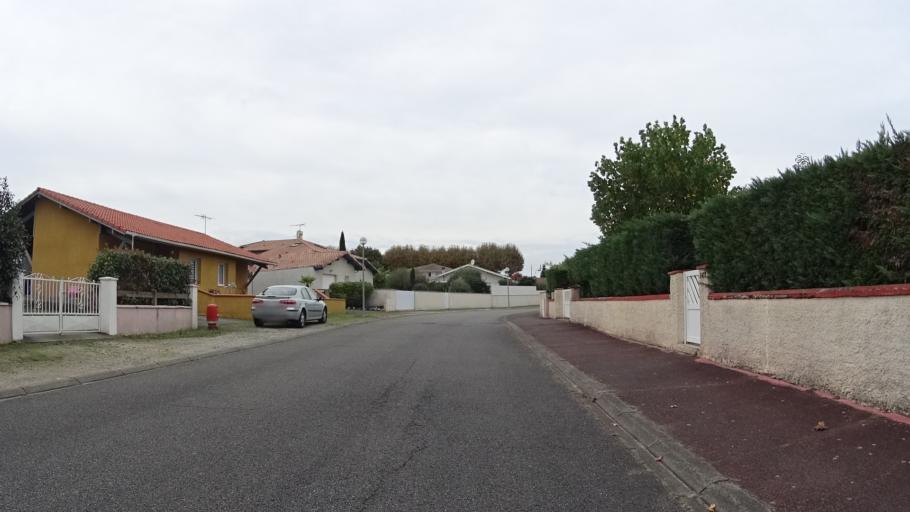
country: FR
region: Aquitaine
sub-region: Departement des Landes
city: Saint-Paul-les-Dax
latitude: 43.7297
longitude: -1.0852
